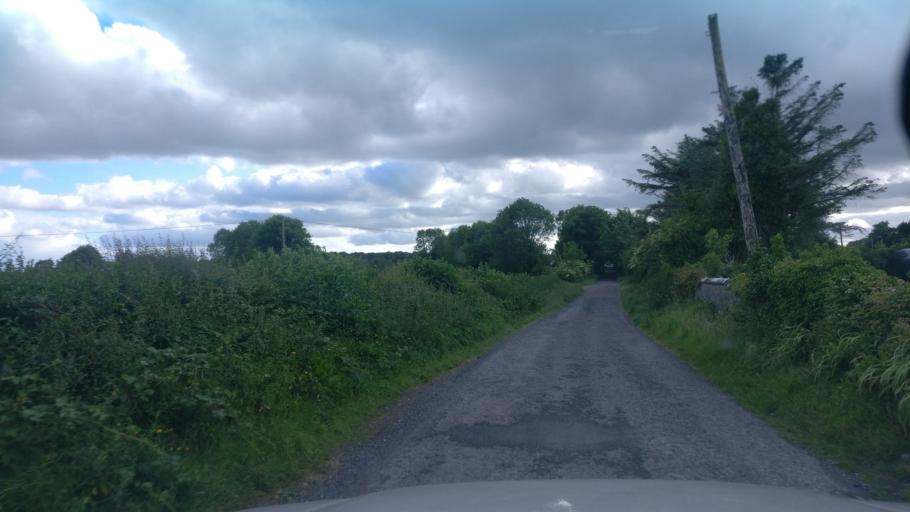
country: IE
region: Connaught
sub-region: County Galway
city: Portumna
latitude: 53.1894
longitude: -8.3207
